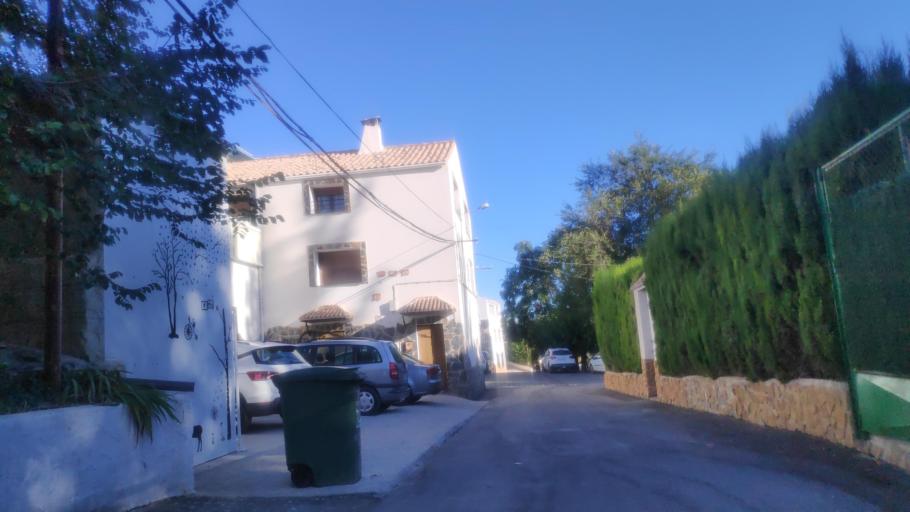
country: ES
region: Andalusia
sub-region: Provincia de Jaen
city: Pozo Alcon
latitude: 37.6731
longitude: -2.9724
